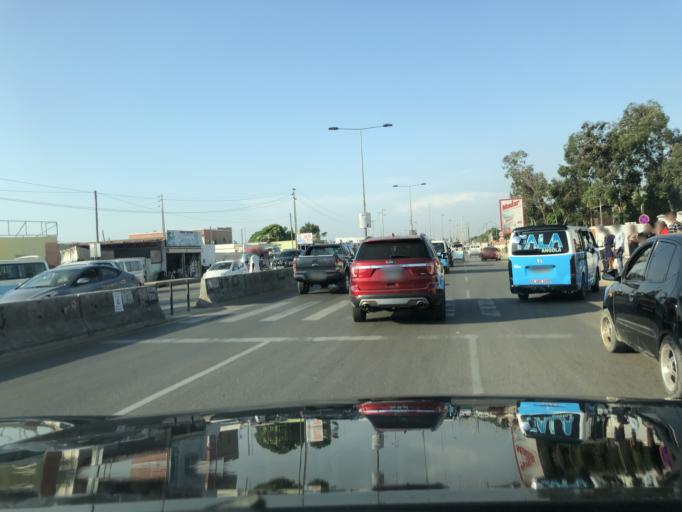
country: AO
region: Luanda
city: Luanda
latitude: -8.9117
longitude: 13.1771
